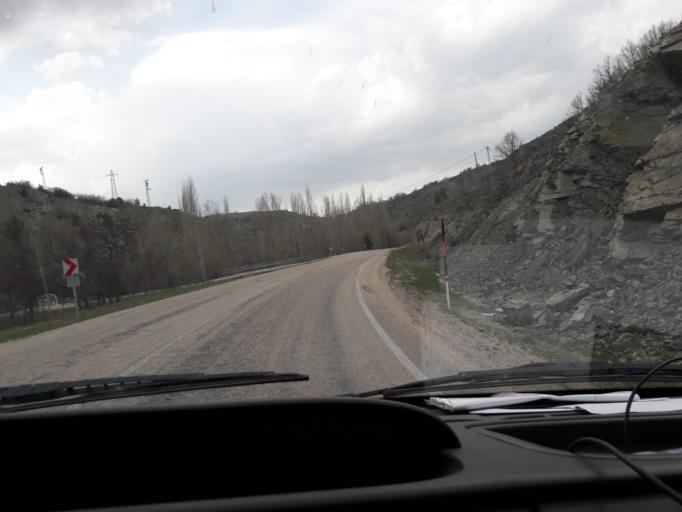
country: TR
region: Giresun
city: Alucra
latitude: 40.2919
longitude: 38.8082
